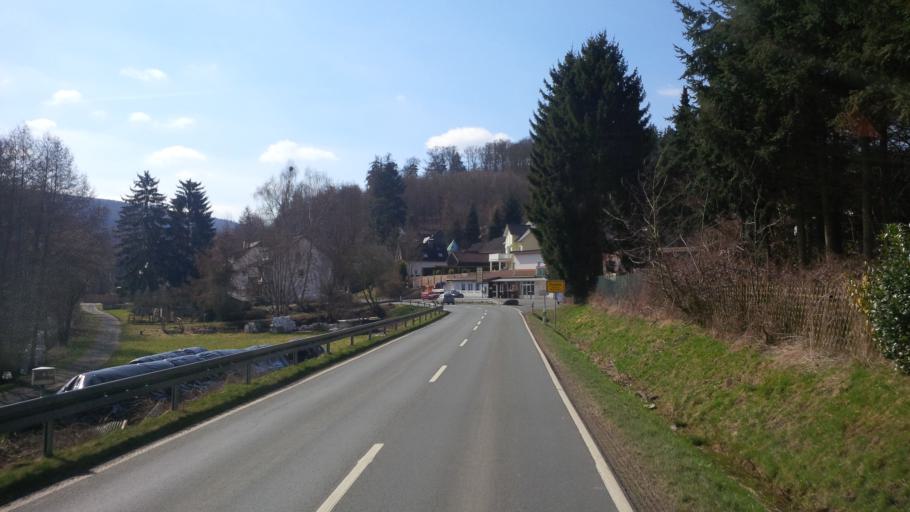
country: DE
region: Hesse
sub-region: Regierungsbezirk Darmstadt
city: Schmitten
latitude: 50.2913
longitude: 8.4612
